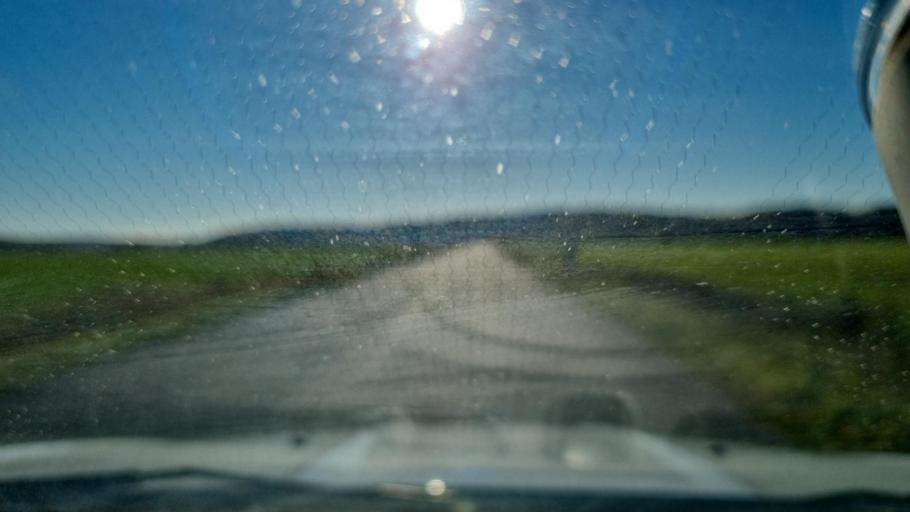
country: SE
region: Uppsala
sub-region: Uppsala Kommun
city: Uppsala
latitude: 59.8400
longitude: 17.6695
